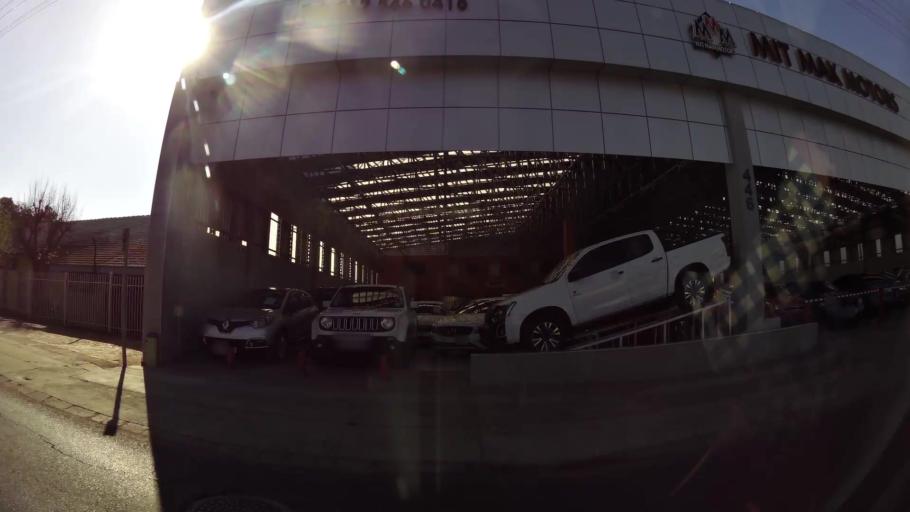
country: ZA
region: Gauteng
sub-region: City of Tshwane Metropolitan Municipality
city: Pretoria
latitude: -25.6778
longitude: 28.1776
